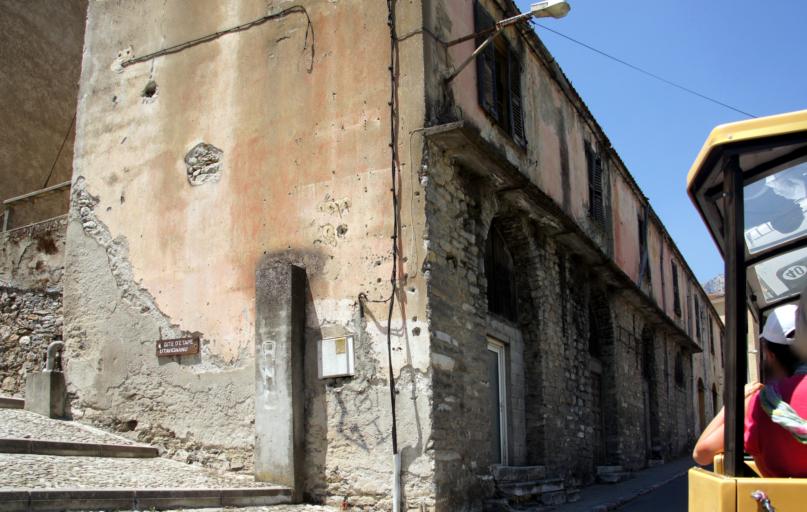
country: FR
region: Corsica
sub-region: Departement de la Haute-Corse
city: Corte
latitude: 42.3032
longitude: 9.1580
